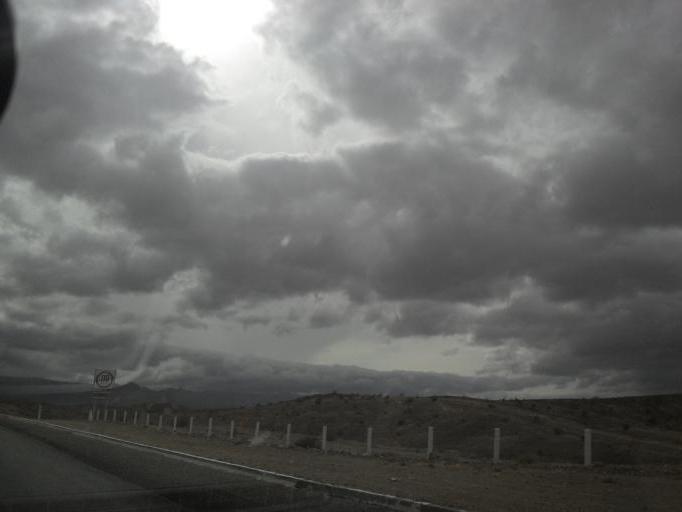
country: MX
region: Baja California
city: Progreso
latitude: 32.5662
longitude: -115.8597
